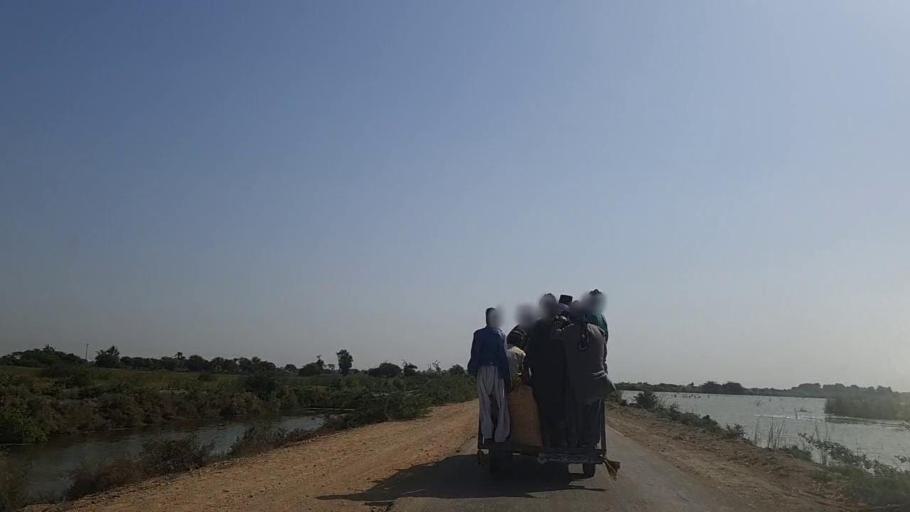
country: PK
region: Sindh
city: Mirpur Batoro
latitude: 24.6494
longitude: 68.2888
